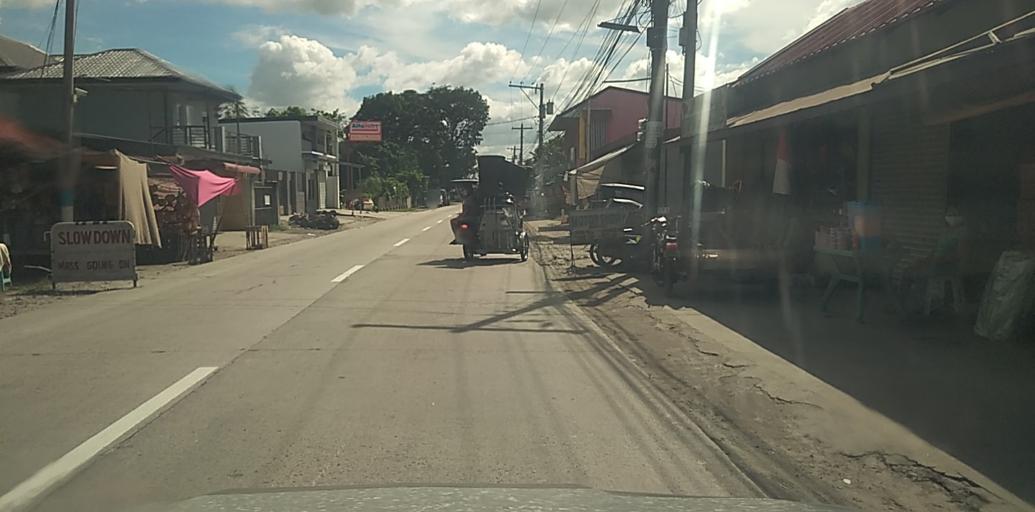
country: PH
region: Central Luzon
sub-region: Province of Pampanga
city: Buensuseso
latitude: 15.1938
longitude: 120.6731
